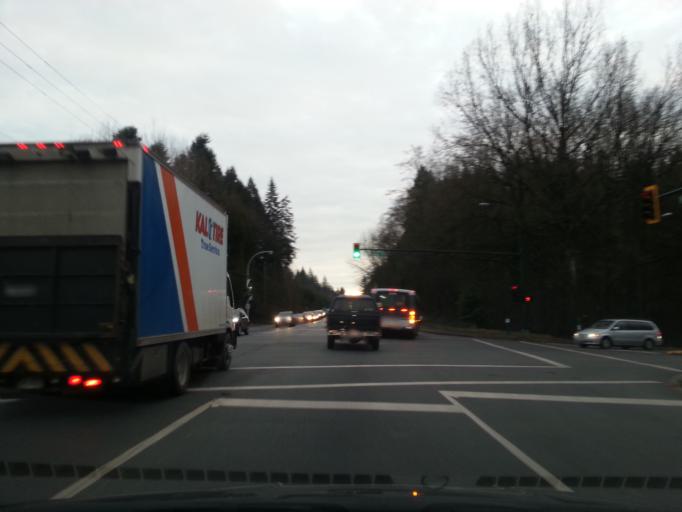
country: CA
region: British Columbia
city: Surrey
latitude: 49.1789
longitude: -122.8347
